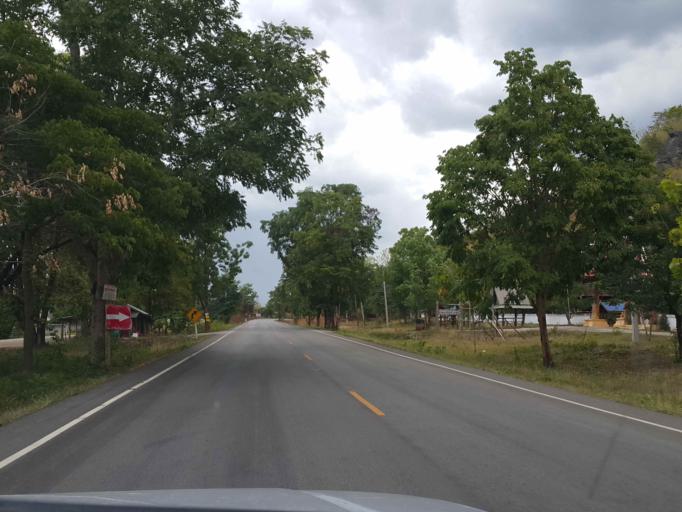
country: TH
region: Sukhothai
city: Thung Saliam
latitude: 17.3465
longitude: 99.4406
